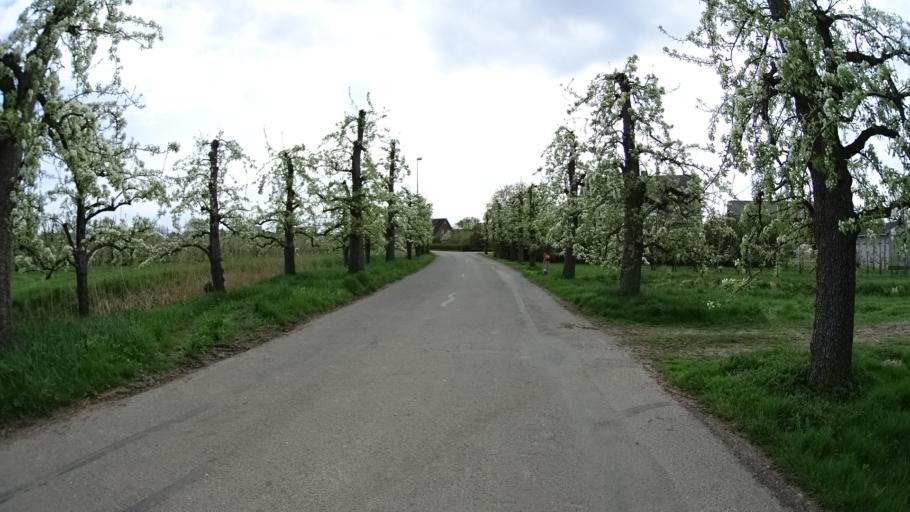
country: DE
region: Lower Saxony
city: Jork
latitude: 53.5349
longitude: 9.7384
